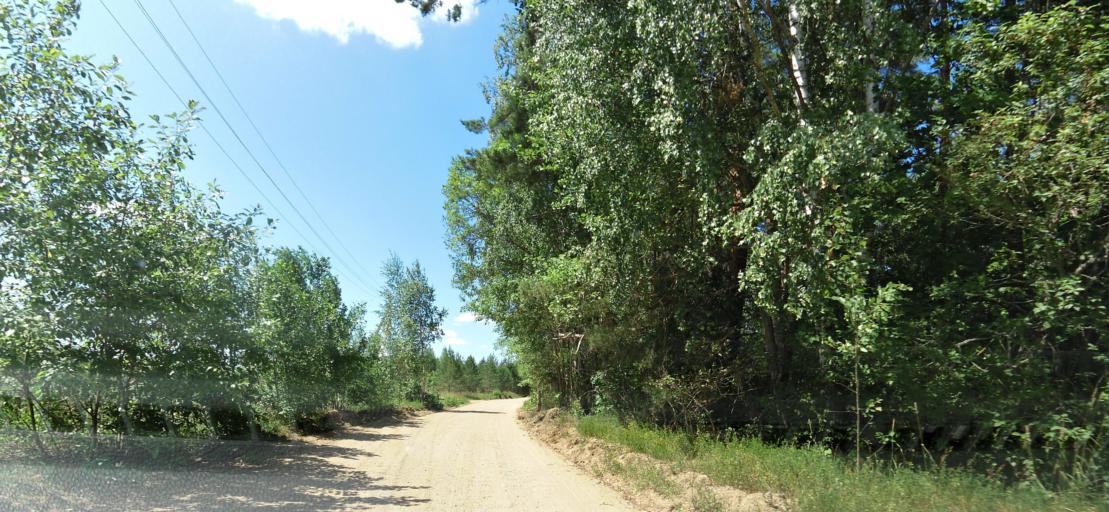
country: LT
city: Nemencine
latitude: 54.8720
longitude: 25.5562
